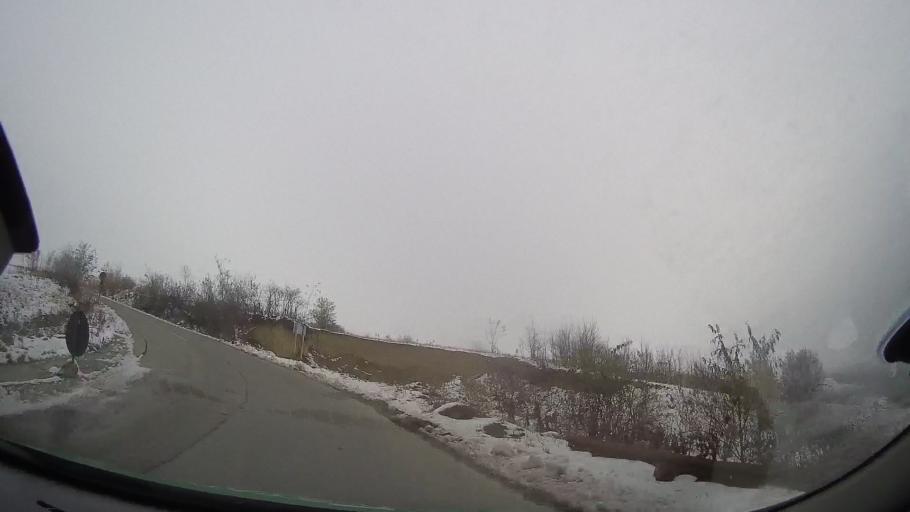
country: RO
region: Bacau
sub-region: Comuna Podu Turcului
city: Podu Turcului
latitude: 46.2026
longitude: 27.3938
